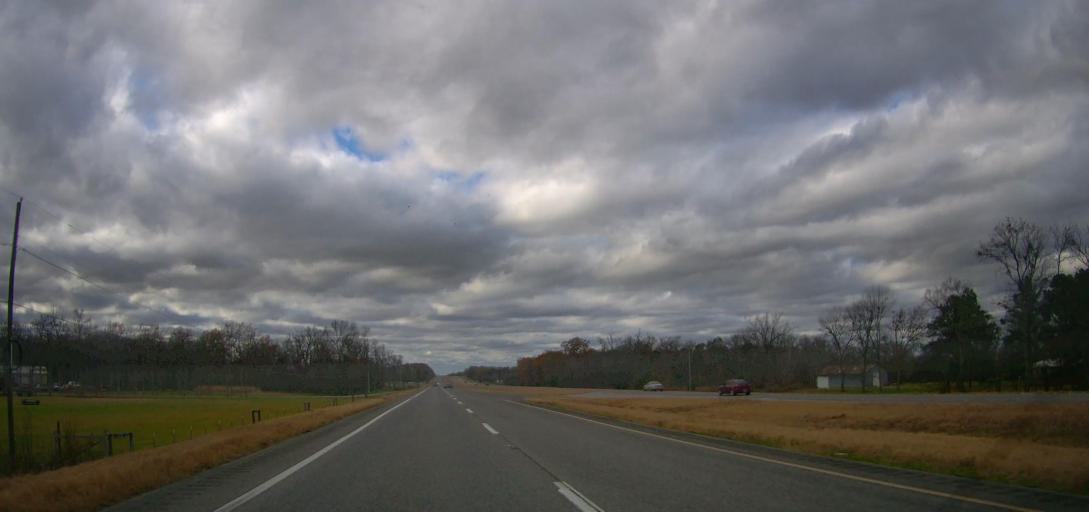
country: US
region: Alabama
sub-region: Morgan County
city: Danville
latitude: 34.4071
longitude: -87.1442
